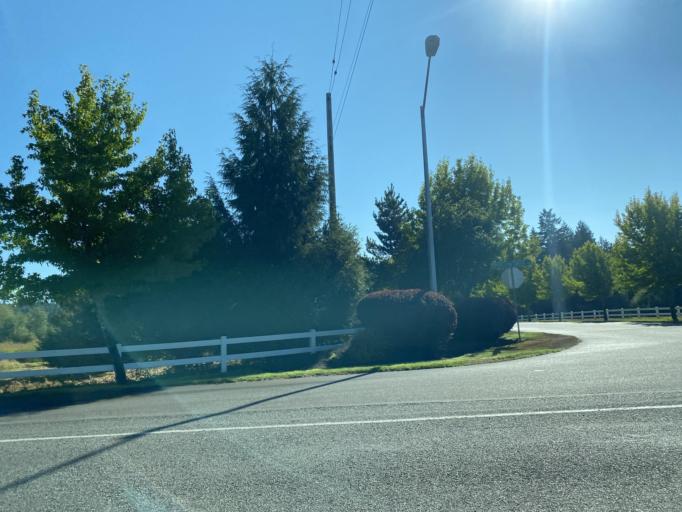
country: US
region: Washington
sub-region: Thurston County
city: Tanglewilde-Thompson Place
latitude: 46.9625
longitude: -122.7628
